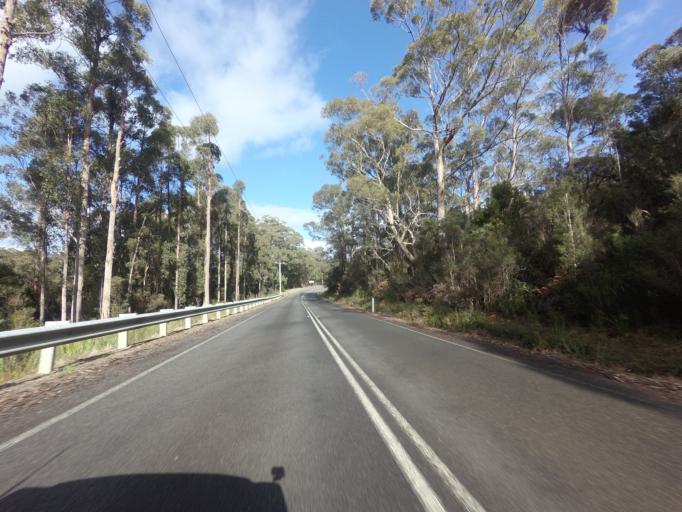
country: AU
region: Tasmania
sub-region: Huon Valley
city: Geeveston
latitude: -43.4156
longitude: 146.9355
